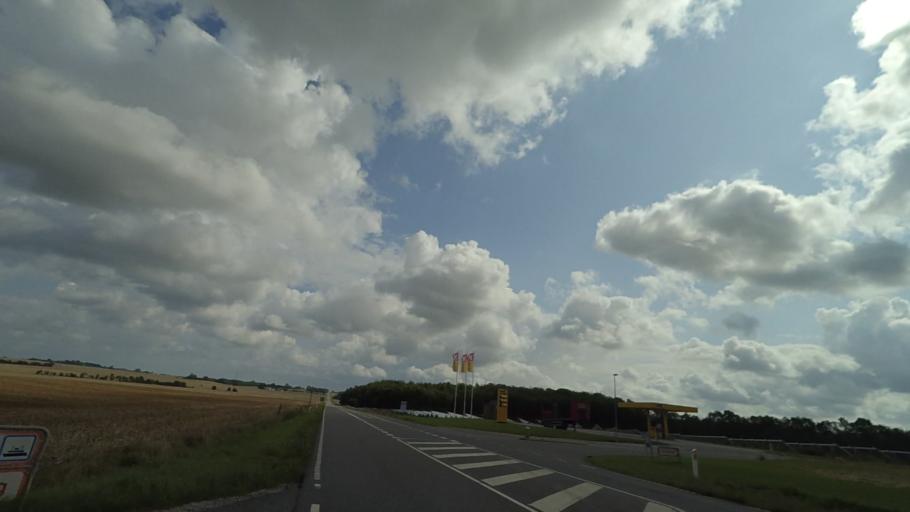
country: DK
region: Central Jutland
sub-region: Norddjurs Kommune
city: Auning
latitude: 56.4875
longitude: 10.4425
